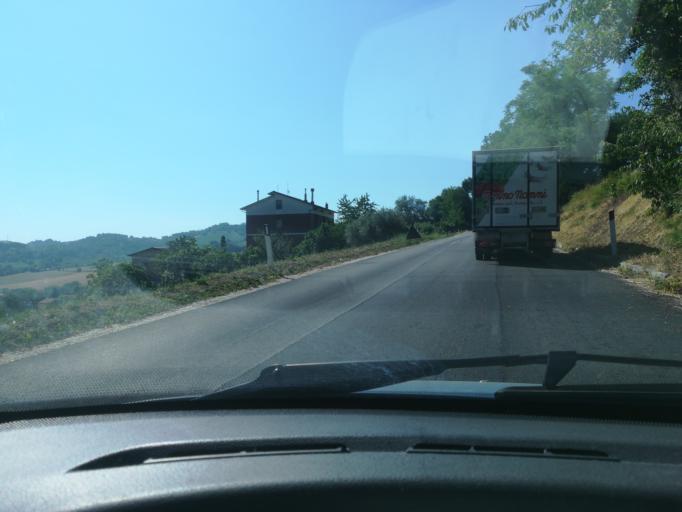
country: IT
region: The Marches
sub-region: Provincia di Macerata
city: Ripe San Ginesio
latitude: 43.1126
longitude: 13.3605
